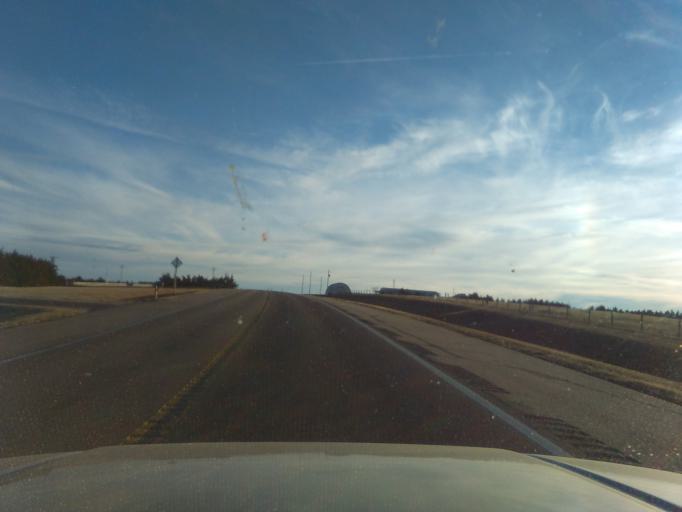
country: US
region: Kansas
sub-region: Logan County
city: Oakley
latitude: 39.1801
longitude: -100.8703
